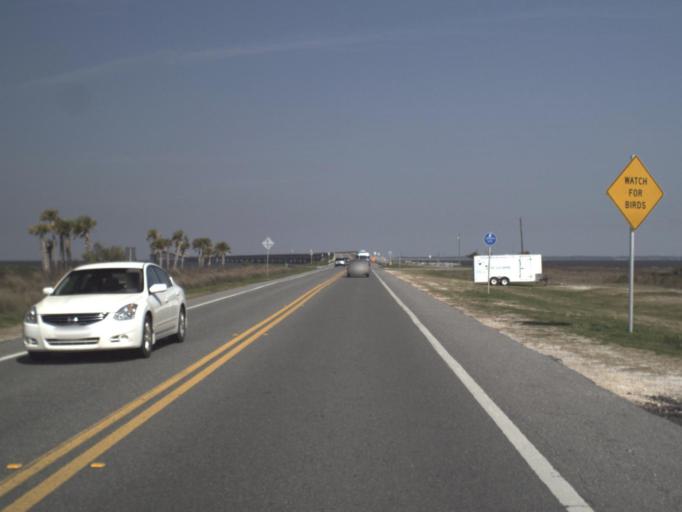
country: US
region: Florida
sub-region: Franklin County
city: Eastpoint
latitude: 29.6668
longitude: -84.8649
